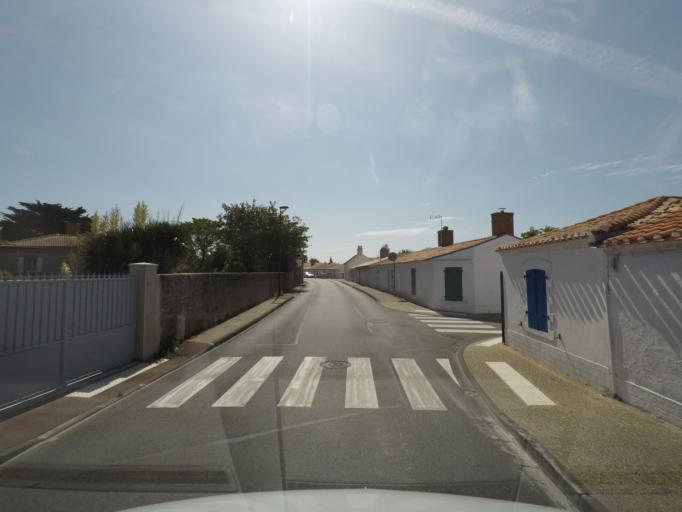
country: FR
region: Pays de la Loire
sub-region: Departement de la Vendee
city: Beauvoir-sur-Mer
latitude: 46.9135
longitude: -2.0396
